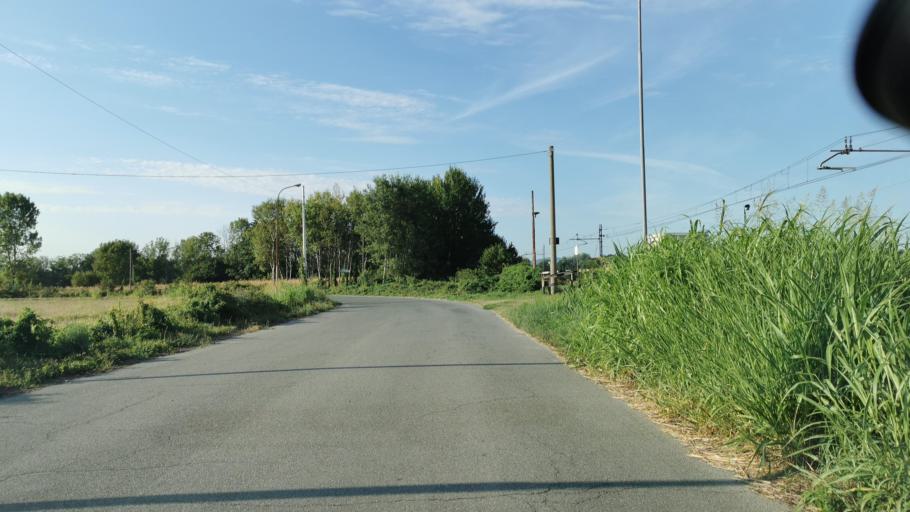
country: IT
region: Piedmont
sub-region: Provincia di Torino
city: Volpiano
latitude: 45.1760
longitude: 7.7743
